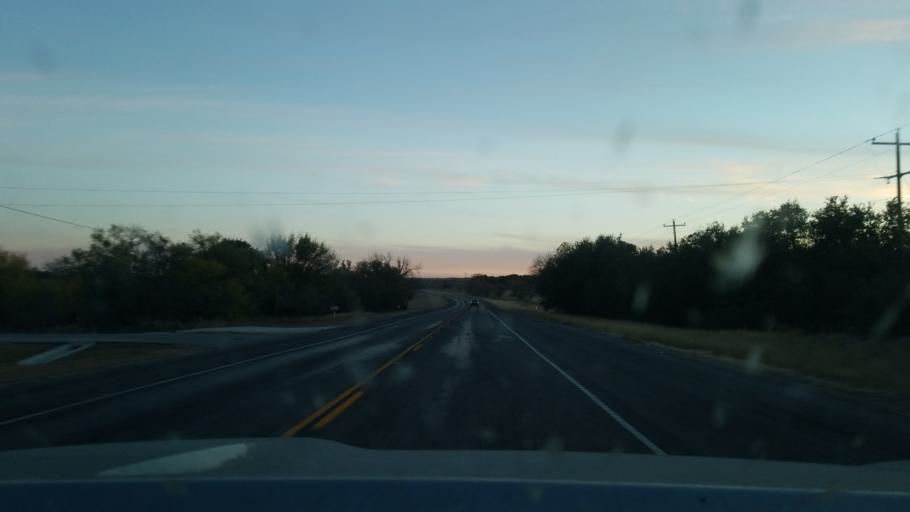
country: US
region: Texas
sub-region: Stephens County
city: Breckenridge
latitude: 32.6000
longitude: -98.9001
